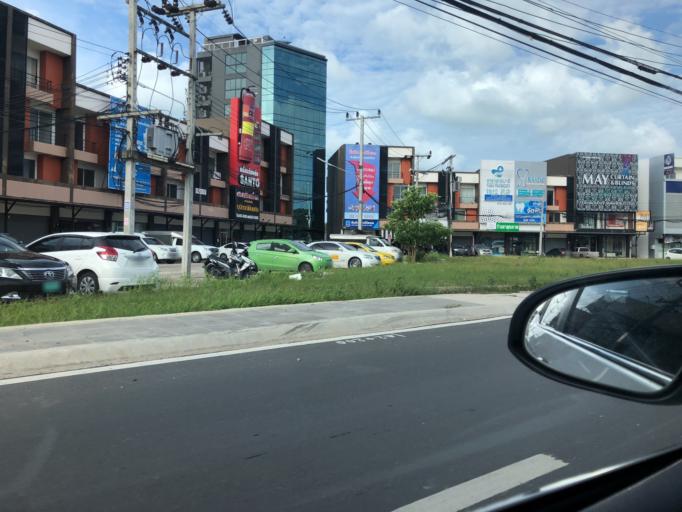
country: TH
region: Phuket
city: Ban Ko Kaeo
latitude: 7.9564
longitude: 98.3875
